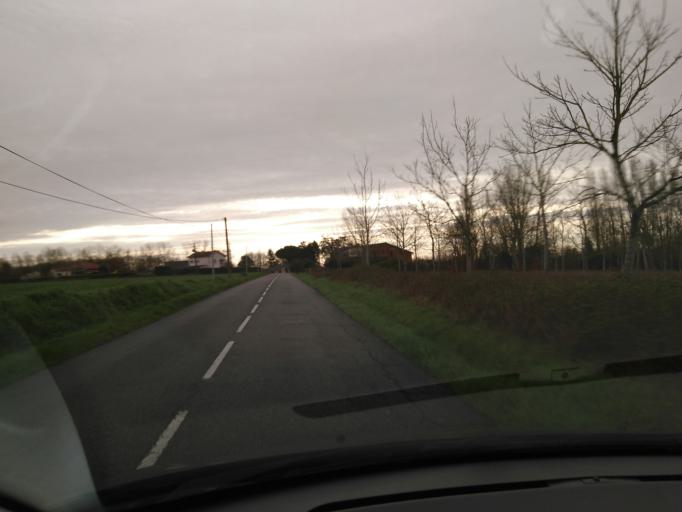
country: FR
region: Midi-Pyrenees
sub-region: Departement de la Haute-Garonne
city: Cepet
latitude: 43.7536
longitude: 1.4532
